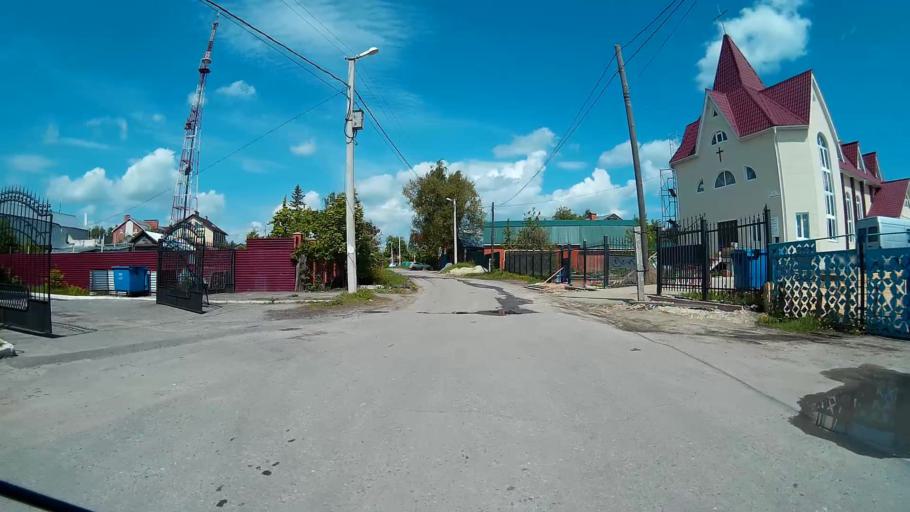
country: RU
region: Ulyanovsk
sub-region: Ulyanovskiy Rayon
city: Ulyanovsk
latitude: 54.3396
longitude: 48.3839
